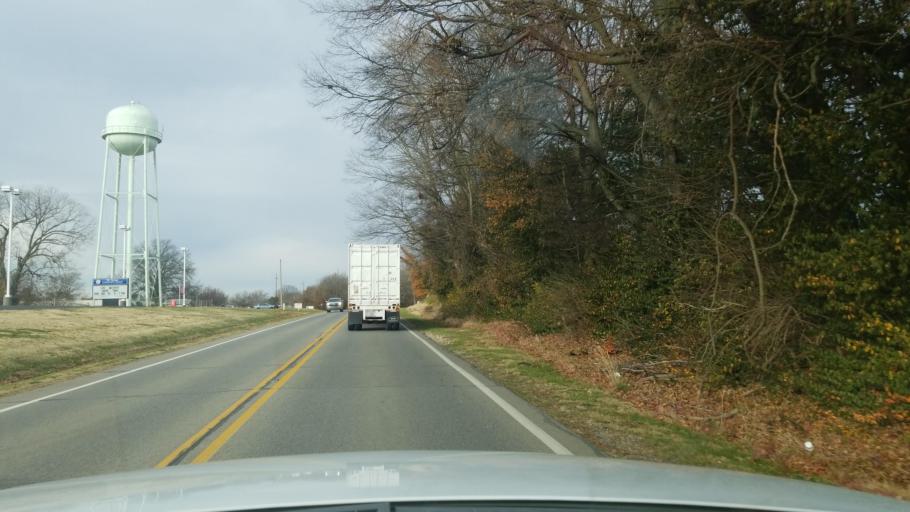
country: US
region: Indiana
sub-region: Posey County
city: Mount Vernon
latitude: 37.9283
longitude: -87.9196
